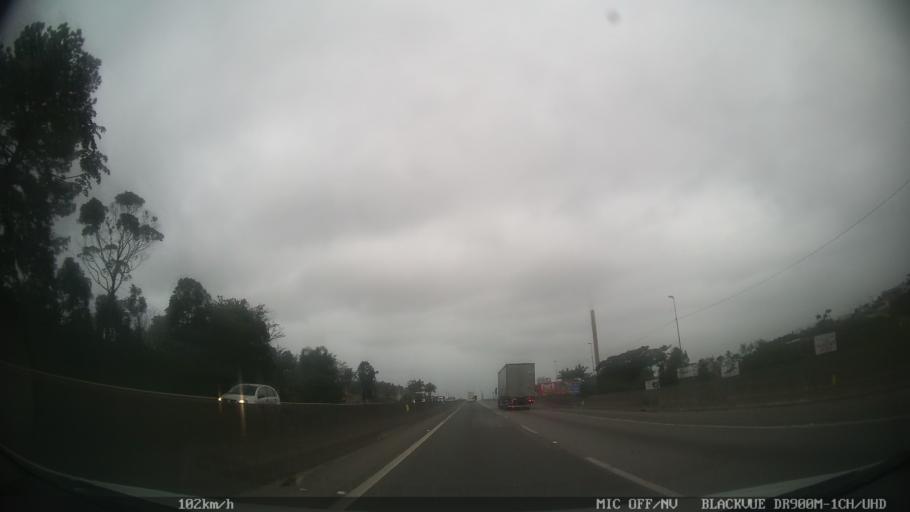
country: BR
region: Santa Catarina
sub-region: Barra Velha
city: Barra Velha
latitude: -26.6271
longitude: -48.7093
